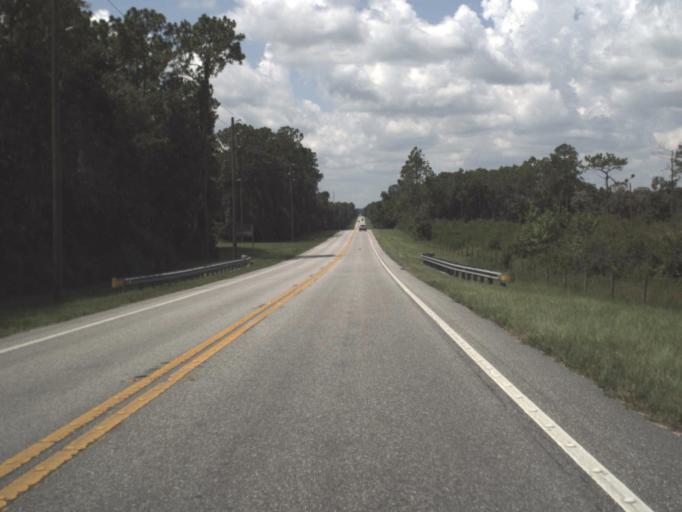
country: US
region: Florida
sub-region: Hernando County
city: North Brooksville
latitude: 28.6235
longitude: -82.3492
